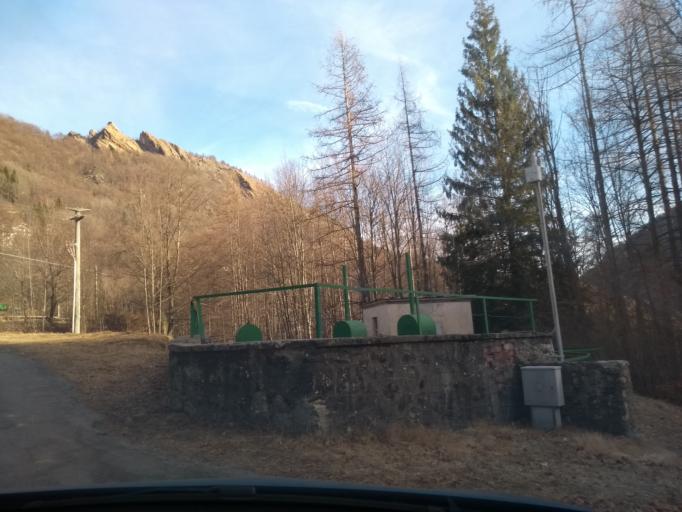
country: IT
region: Piedmont
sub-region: Provincia di Torino
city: Ala di Stura
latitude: 45.3127
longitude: 7.3096
